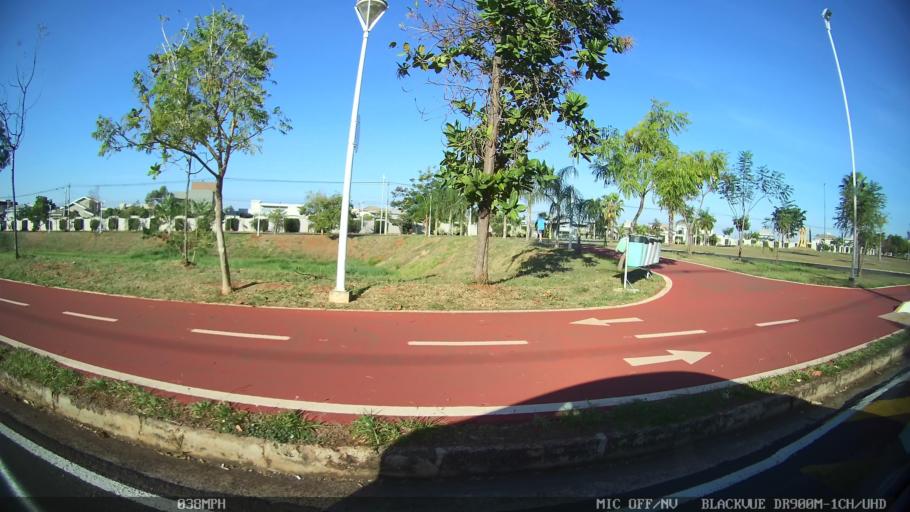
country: BR
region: Sao Paulo
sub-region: Sao Jose Do Rio Preto
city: Sao Jose do Rio Preto
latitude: -20.8599
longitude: -49.4124
